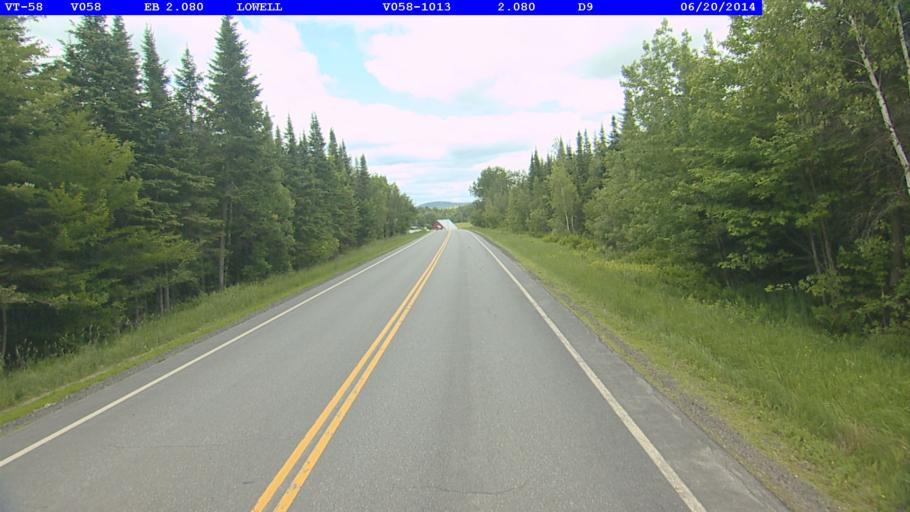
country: US
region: Vermont
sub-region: Orleans County
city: Newport
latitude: 44.8067
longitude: -72.4133
